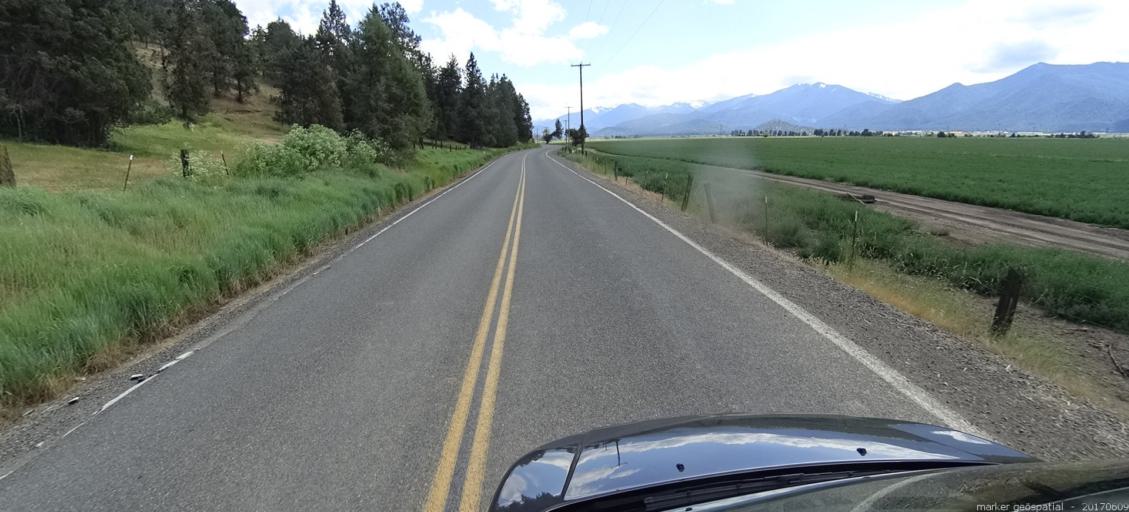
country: US
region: California
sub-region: Siskiyou County
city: Yreka
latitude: 41.5137
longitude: -122.8400
